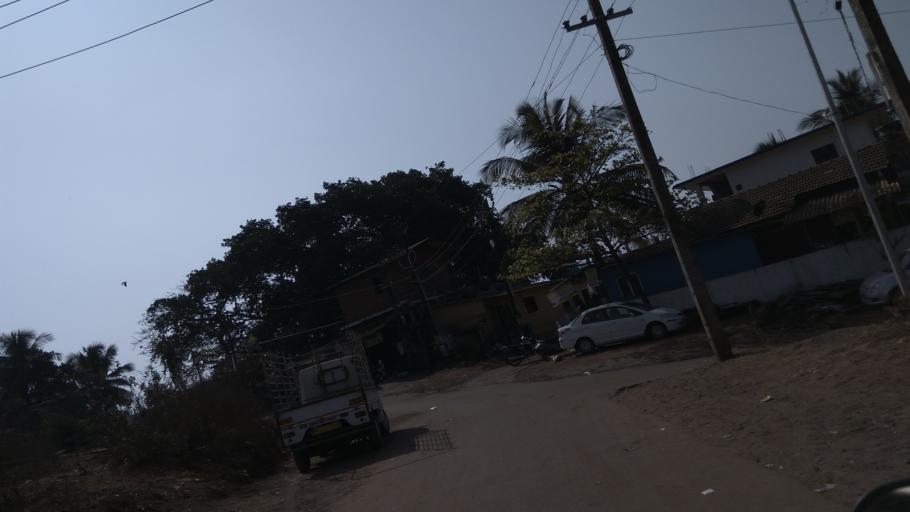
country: IN
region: Goa
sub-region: North Goa
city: Candolim
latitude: 15.5247
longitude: 73.7716
